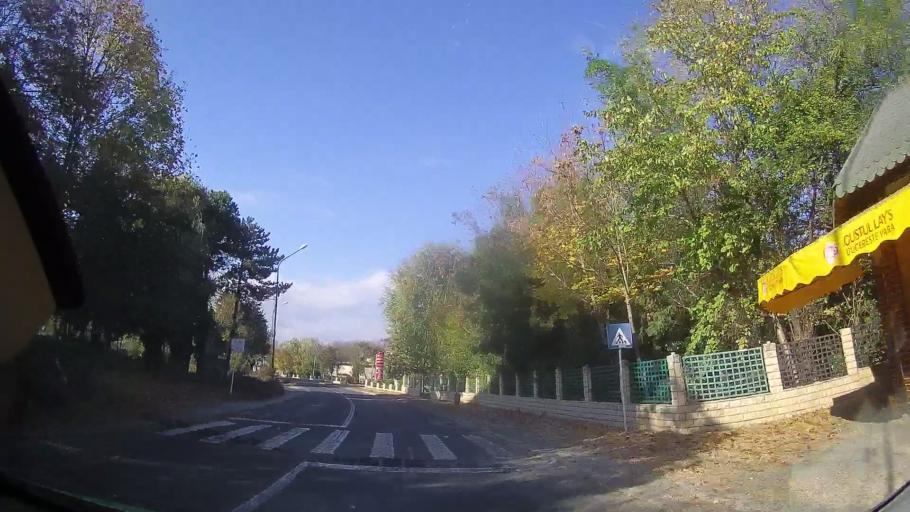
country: RO
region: Constanta
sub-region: Comuna Douazeci si Trei August
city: Douazeci si Trei August
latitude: 43.8588
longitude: 28.6025
